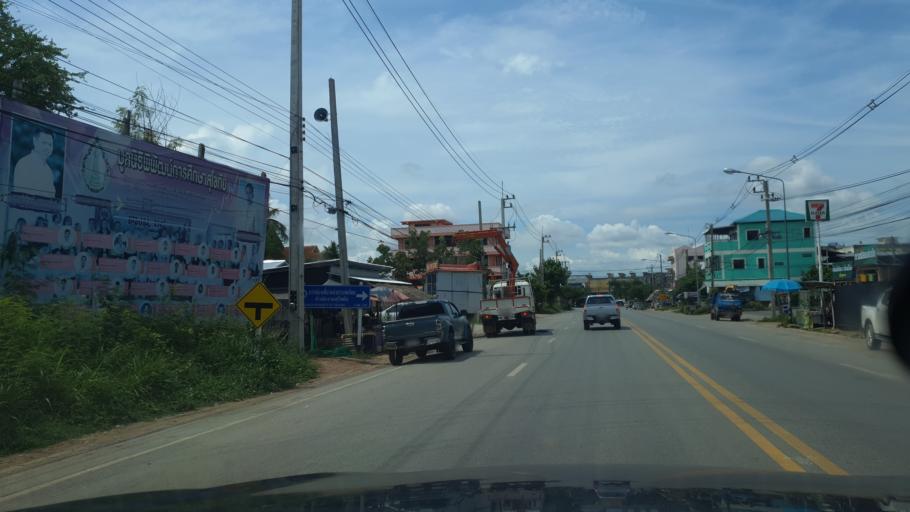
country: TH
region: Sukhothai
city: Sukhothai
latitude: 17.0243
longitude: 99.8161
